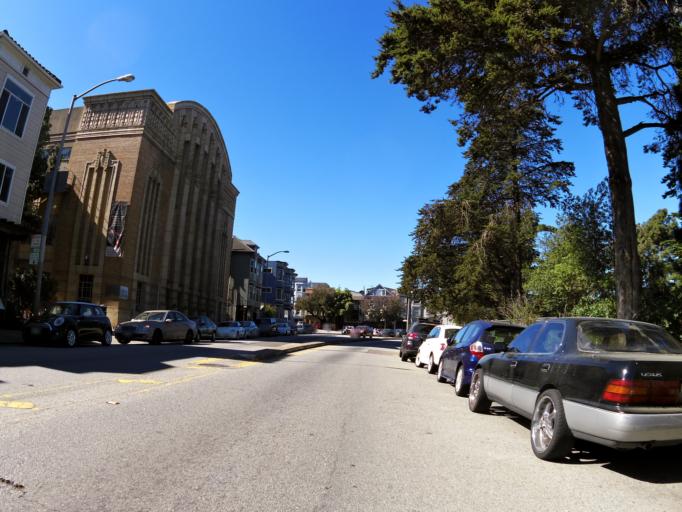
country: US
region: California
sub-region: San Francisco County
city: San Francisco
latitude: 37.7660
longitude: -122.4566
